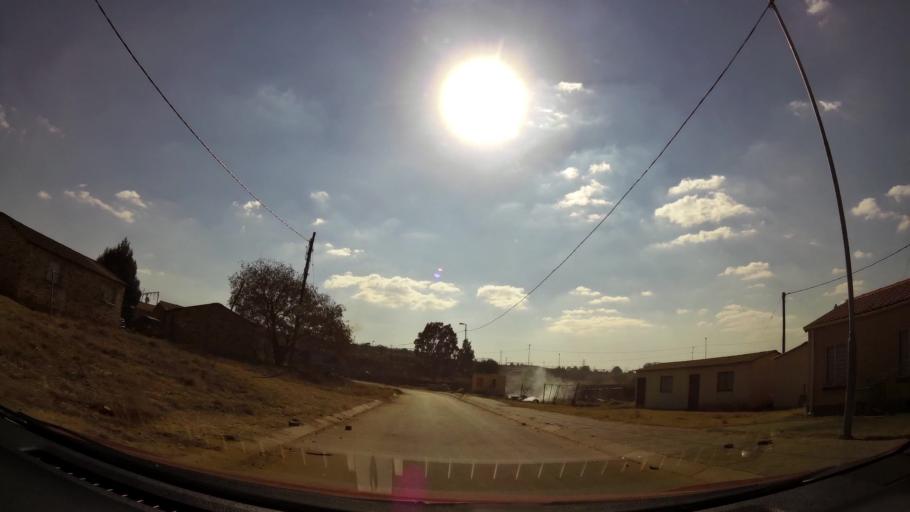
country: ZA
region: Gauteng
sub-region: City of Johannesburg Metropolitan Municipality
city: Soweto
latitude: -26.2233
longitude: 27.9261
